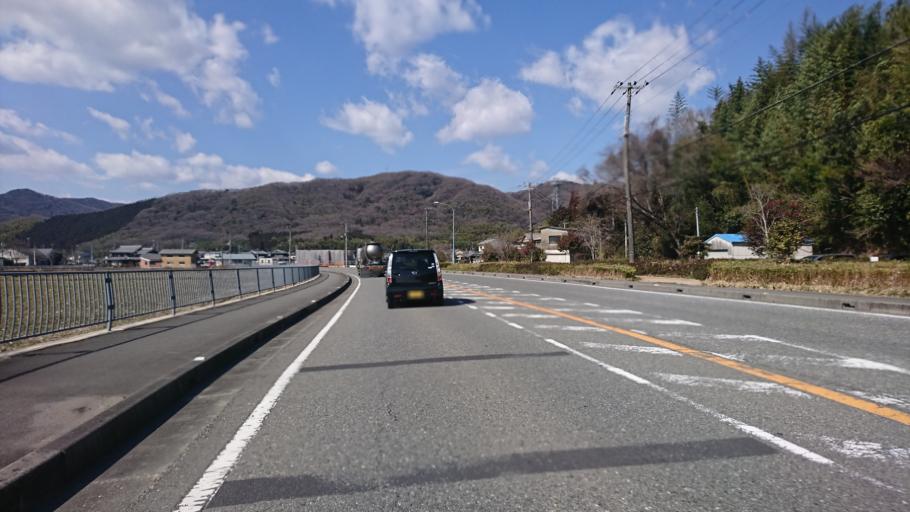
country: JP
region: Hyogo
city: Himeji
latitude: 34.8573
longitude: 134.7781
